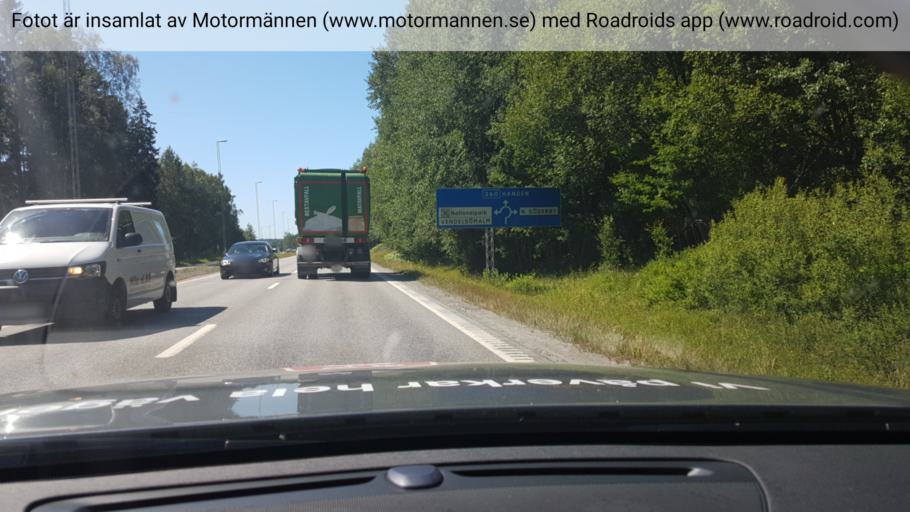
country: SE
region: Stockholm
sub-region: Haninge Kommun
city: Haninge
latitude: 59.1936
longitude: 18.1816
